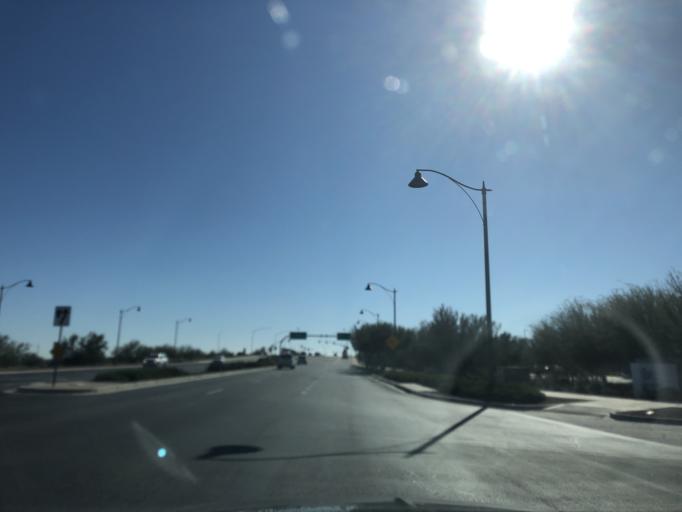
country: US
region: Arizona
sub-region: Maricopa County
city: Citrus Park
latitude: 33.4646
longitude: -112.5045
